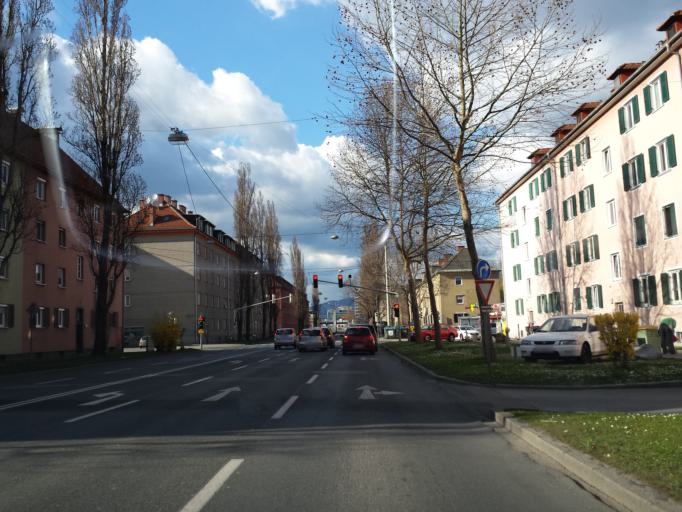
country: AT
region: Styria
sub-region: Graz Stadt
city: Graz
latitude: 47.0512
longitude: 15.4286
